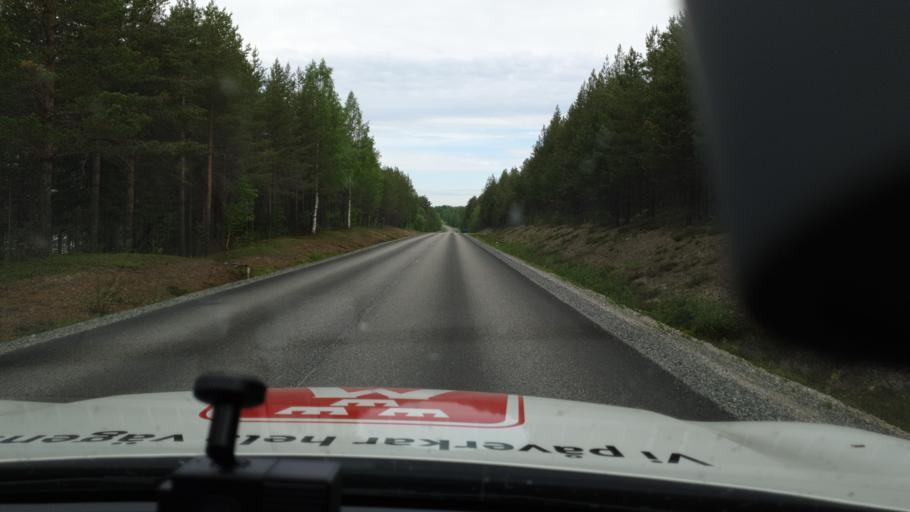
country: SE
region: Vaesterbotten
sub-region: Mala Kommun
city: Mala
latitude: 64.8948
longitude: 18.7133
